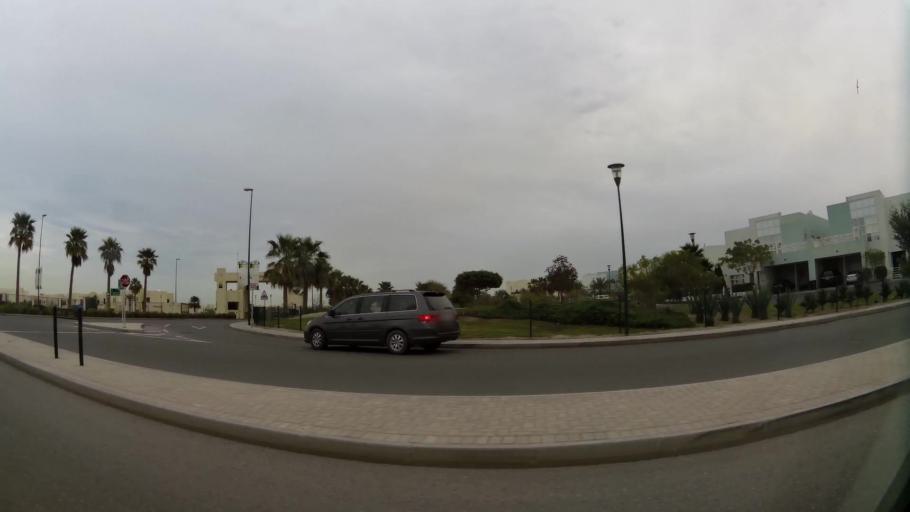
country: BH
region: Northern
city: Ar Rifa'
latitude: 26.1023
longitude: 50.5654
